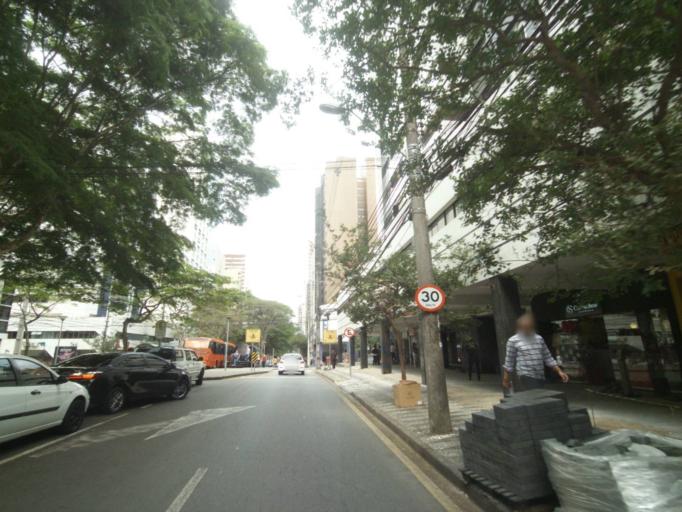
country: BR
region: Parana
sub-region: Curitiba
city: Curitiba
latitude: -25.4336
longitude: -49.3004
